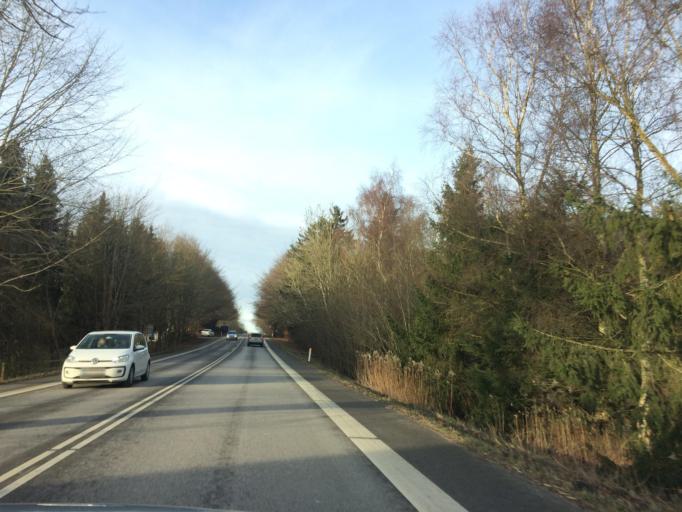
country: DK
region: Capital Region
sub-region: Fredensborg Kommune
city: Fredensborg
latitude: 55.9379
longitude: 12.4322
